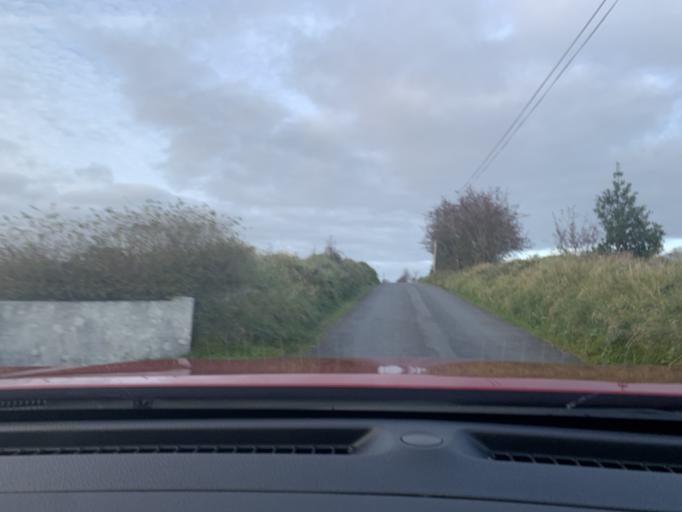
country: IE
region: Connaught
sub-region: Roscommon
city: Ballaghaderreen
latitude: 53.9777
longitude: -8.6185
